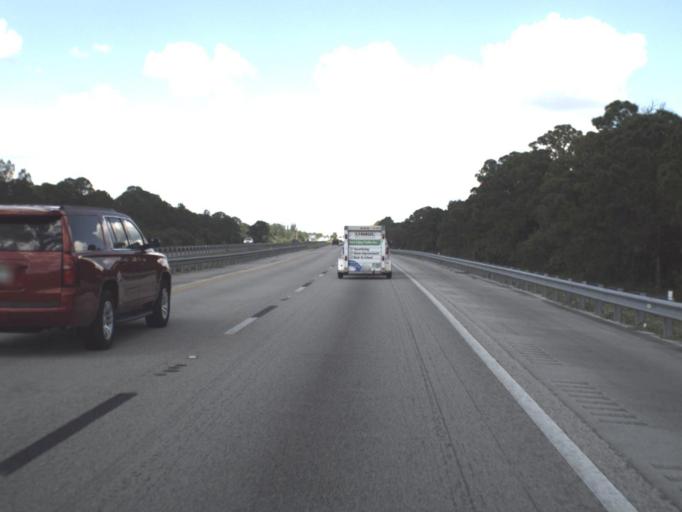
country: US
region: Florida
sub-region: Saint Lucie County
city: Lakewood Park
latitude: 27.4609
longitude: -80.4334
